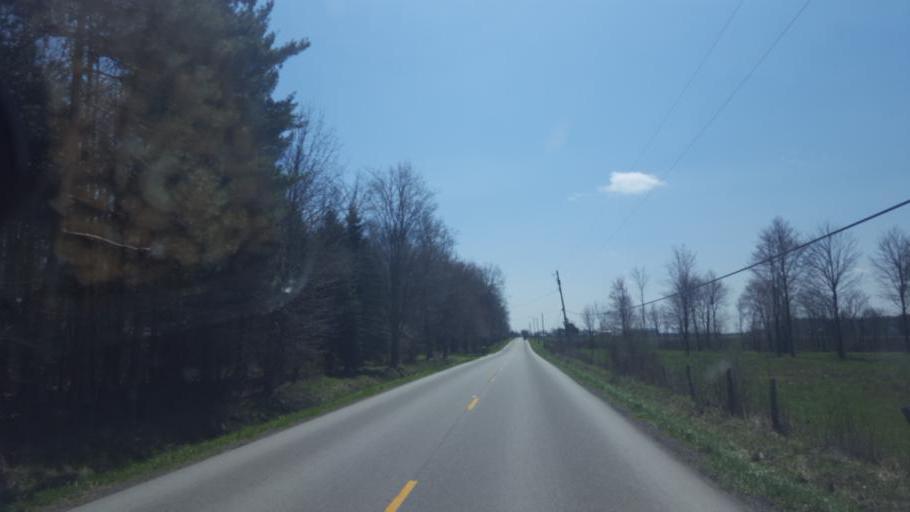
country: US
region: Ohio
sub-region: Geauga County
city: Middlefield
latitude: 41.3917
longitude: -81.1084
